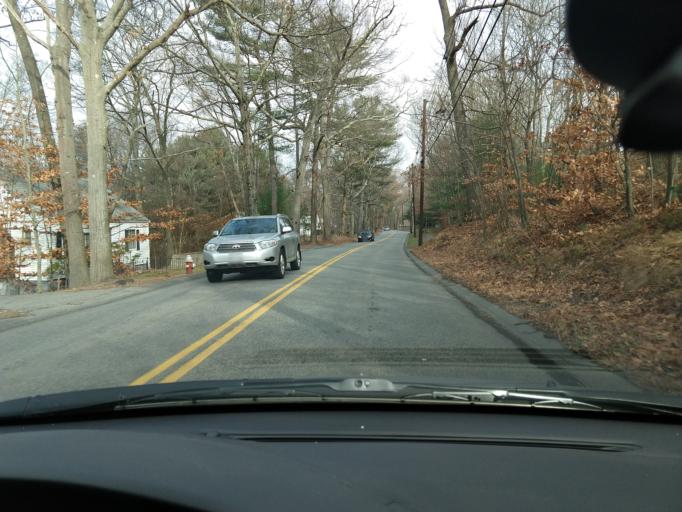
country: US
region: Massachusetts
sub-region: Middlesex County
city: Bedford
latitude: 42.4884
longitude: -71.2581
